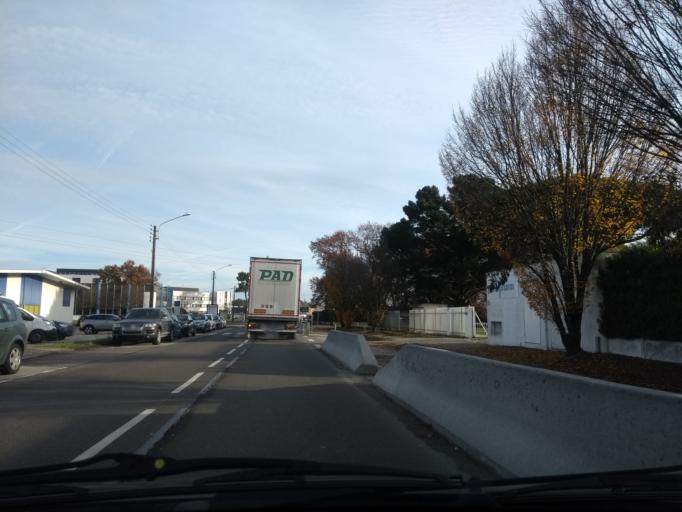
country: FR
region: Aquitaine
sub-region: Departement de la Gironde
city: Canejan
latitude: 44.7846
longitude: -0.6451
